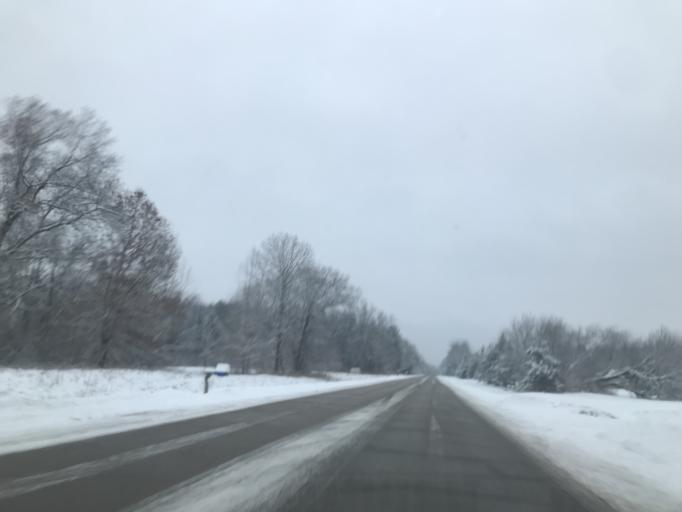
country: US
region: Wisconsin
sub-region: Oconto County
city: Oconto Falls
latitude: 44.8616
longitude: -88.1070
